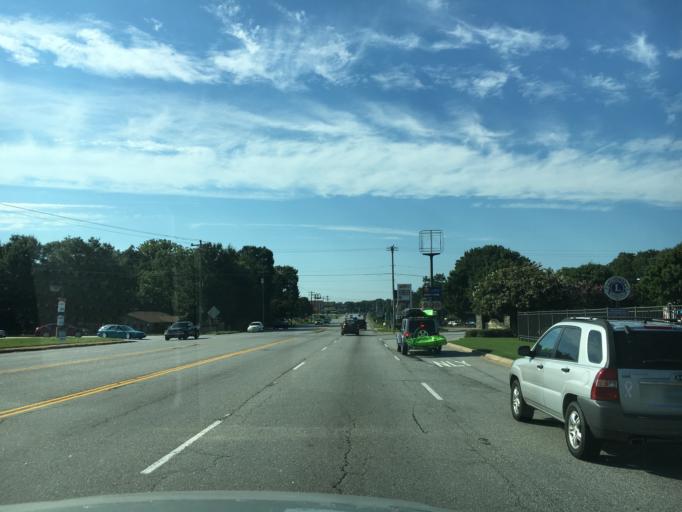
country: US
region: South Carolina
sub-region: Spartanburg County
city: Valley Falls
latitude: 35.0139
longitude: -81.9588
